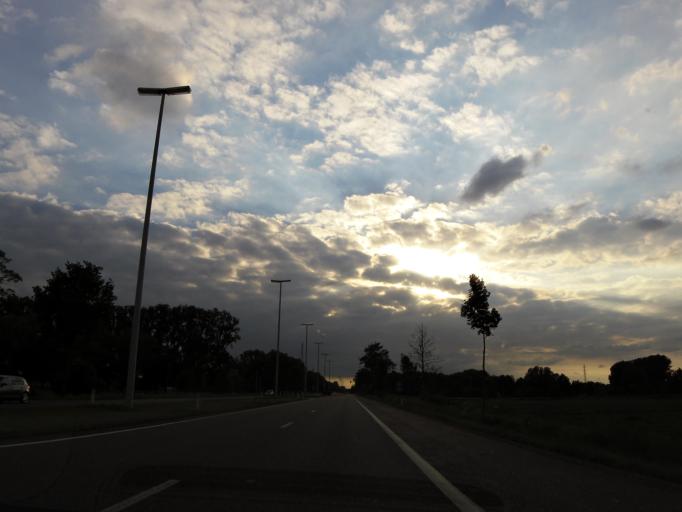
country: BE
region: Flanders
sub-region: Provincie Limburg
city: Hasselt
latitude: 50.9300
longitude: 5.3798
